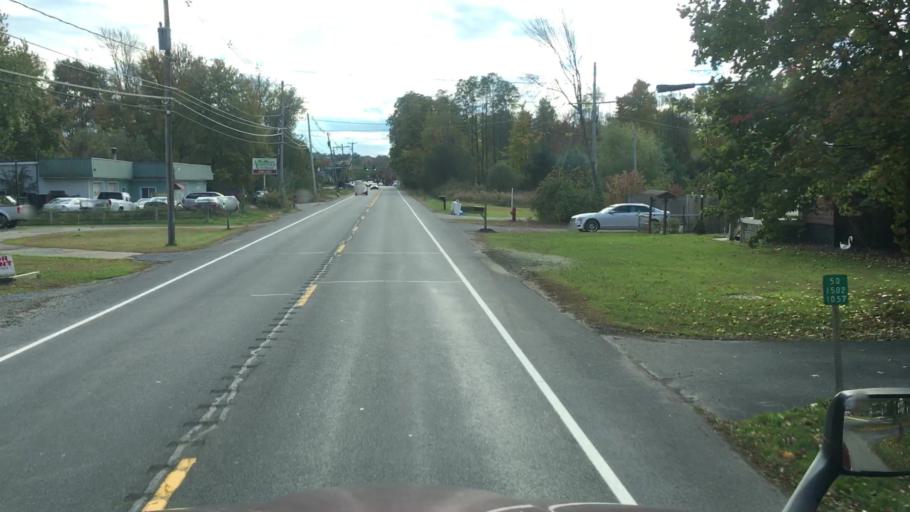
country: US
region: New York
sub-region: Saratoga County
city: Ballston Spa
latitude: 42.9778
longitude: -73.8604
